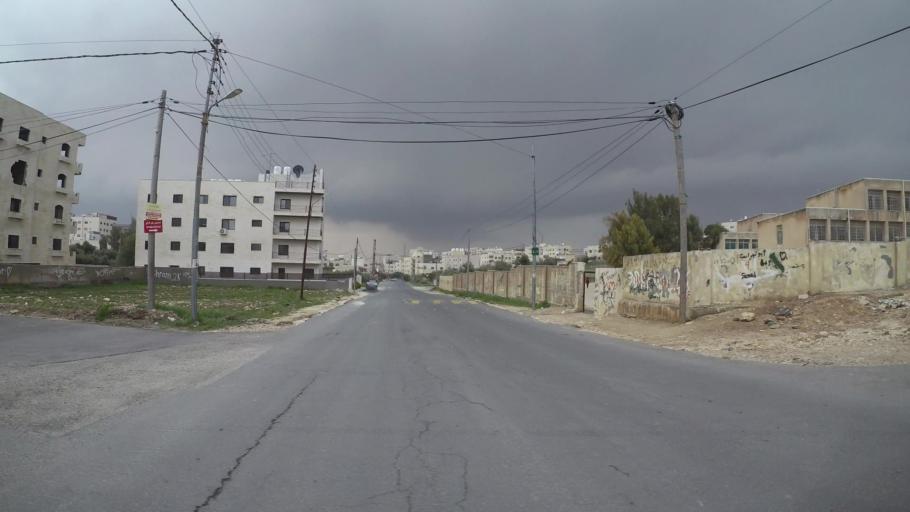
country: JO
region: Amman
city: Umm as Summaq
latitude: 31.8850
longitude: 35.8578
